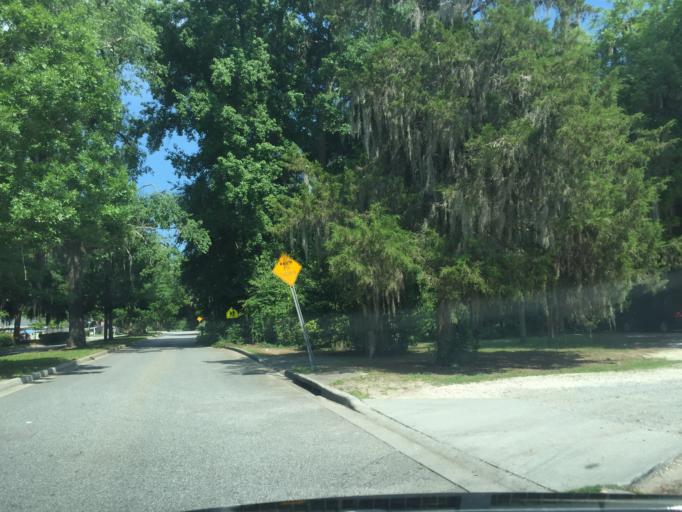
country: US
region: Georgia
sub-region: Chatham County
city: Isle of Hope
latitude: 31.9950
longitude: -81.1043
